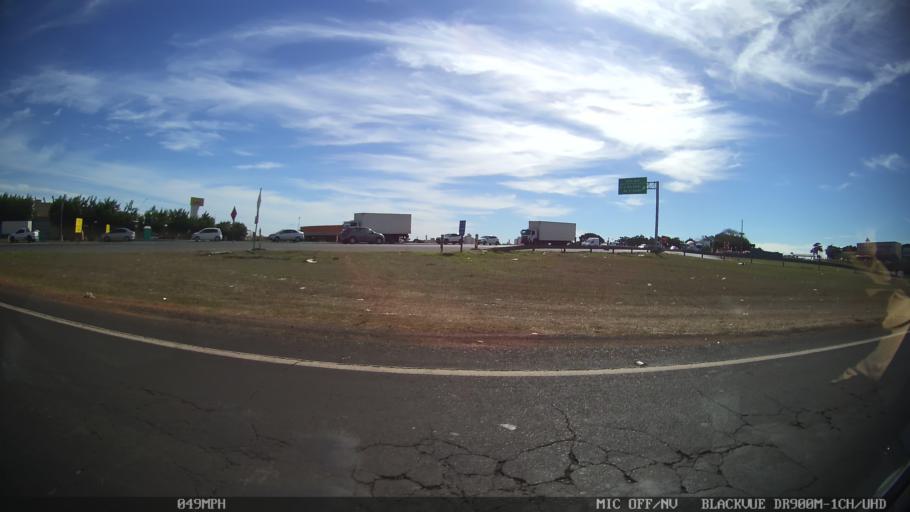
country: BR
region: Sao Paulo
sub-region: Sao Jose Do Rio Preto
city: Sao Jose do Rio Preto
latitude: -20.8036
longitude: -49.3547
